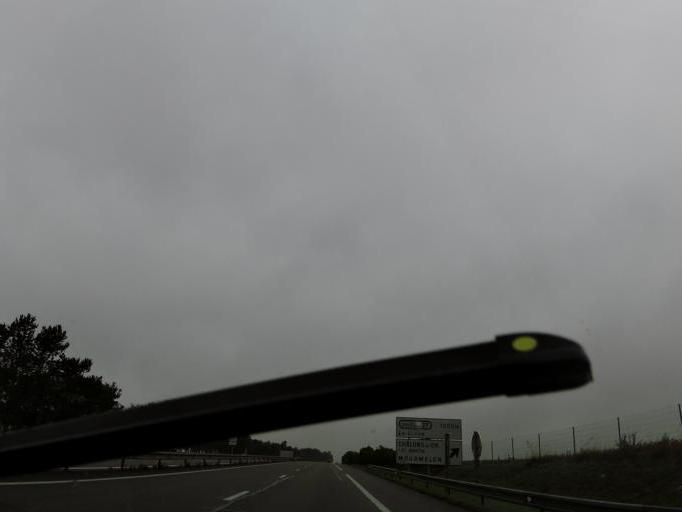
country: FR
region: Champagne-Ardenne
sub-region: Departement de la Marne
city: Fagnieres
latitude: 49.0404
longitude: 4.3378
